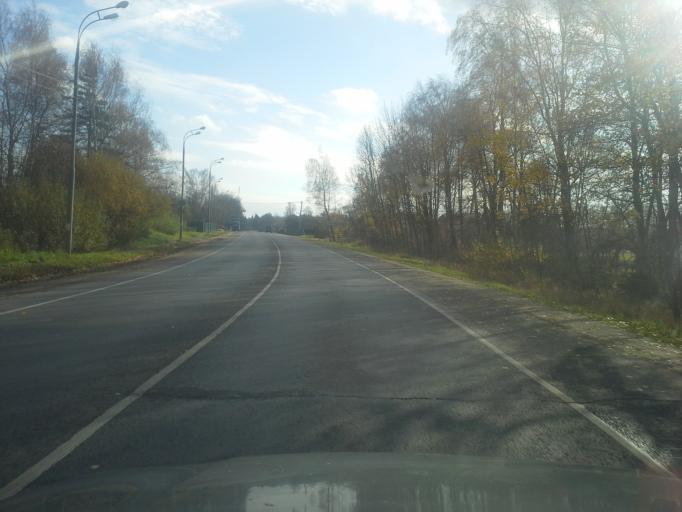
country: RU
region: Moskovskaya
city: Zvenigorod
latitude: 55.6832
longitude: 36.9034
